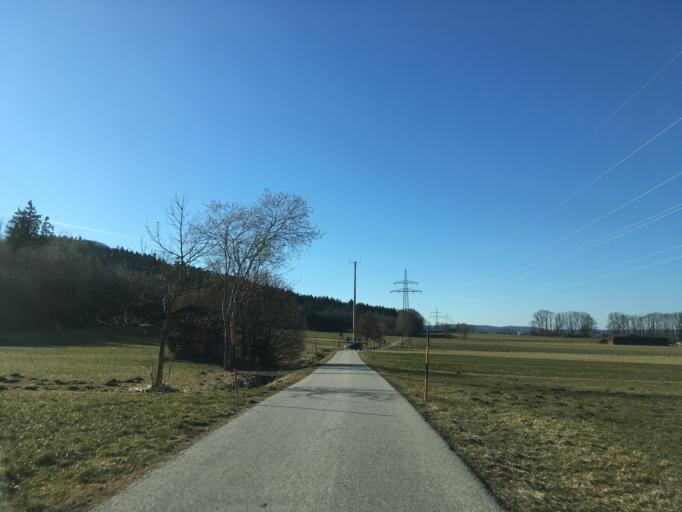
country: DE
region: Bavaria
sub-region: Upper Bavaria
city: Bruckmuhl
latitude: 47.8611
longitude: 11.9207
